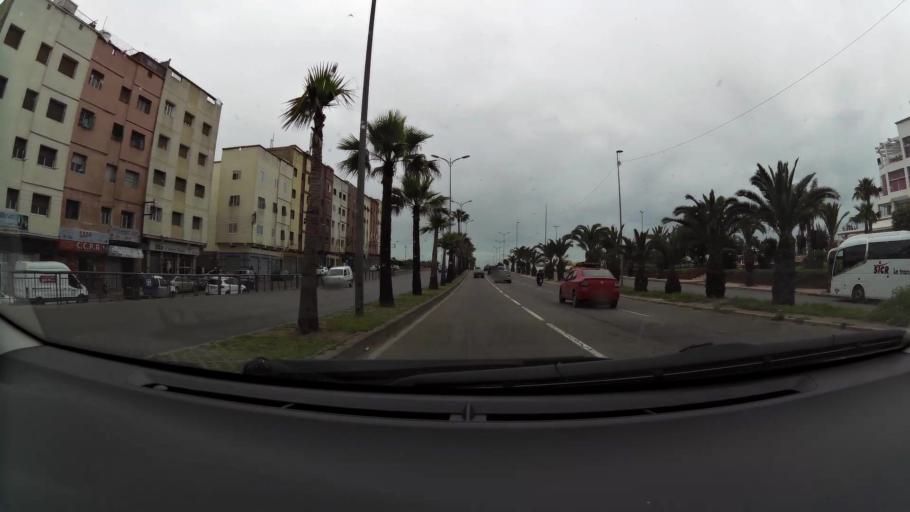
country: MA
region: Grand Casablanca
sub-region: Casablanca
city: Casablanca
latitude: 33.5736
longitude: -7.5824
